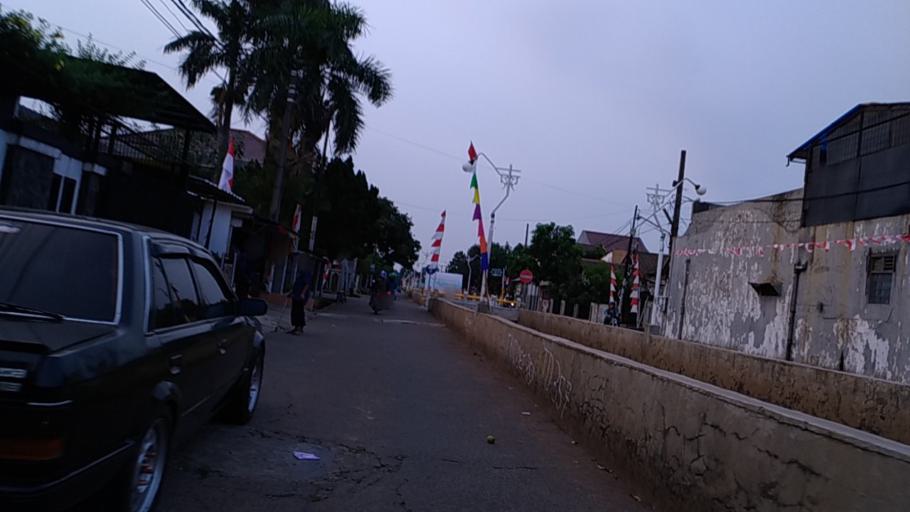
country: ID
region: West Java
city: Depok
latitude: -6.3760
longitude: 106.8583
